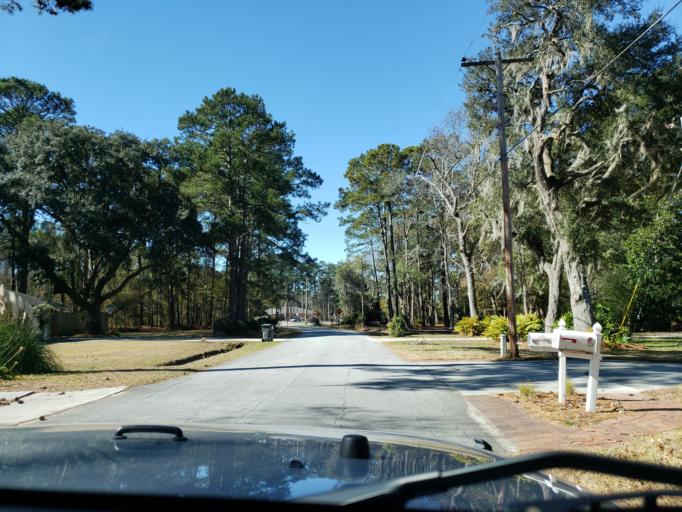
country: US
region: Georgia
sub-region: Chatham County
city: Wilmington Island
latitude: 32.0329
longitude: -80.9794
